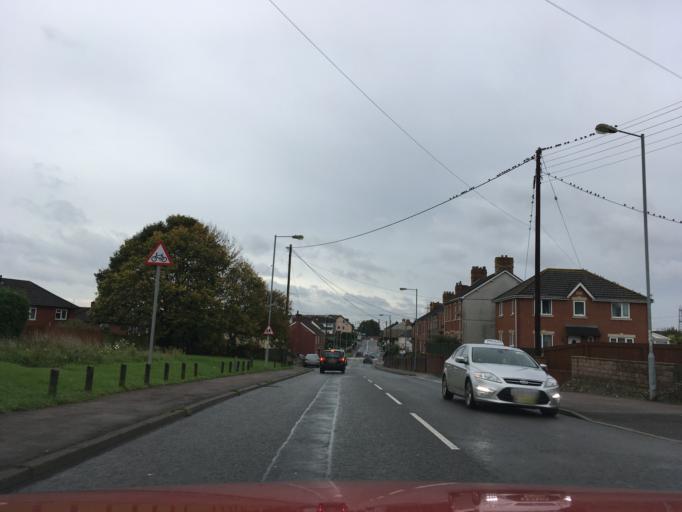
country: GB
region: Wales
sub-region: Monmouthshire
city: Caldicot
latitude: 51.5896
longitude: -2.7608
